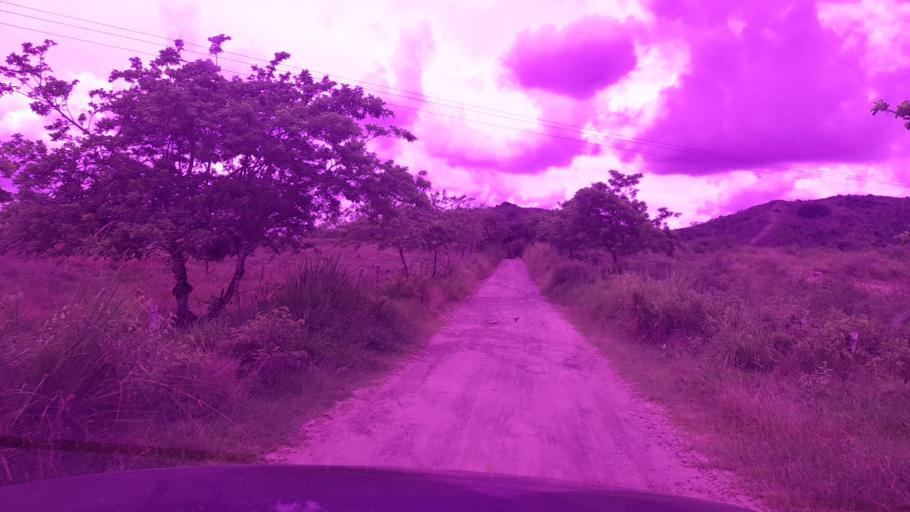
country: CO
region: Valle del Cauca
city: Andalucia
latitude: 4.1759
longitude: -76.1298
